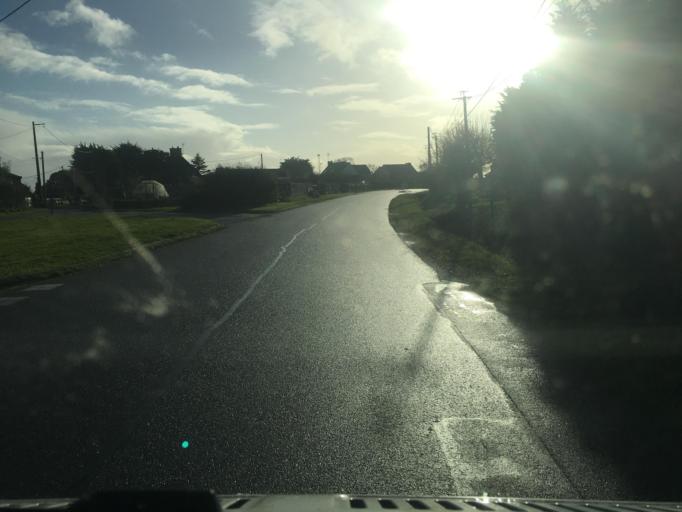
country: FR
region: Brittany
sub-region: Departement du Morbihan
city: Surzur
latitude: 47.5225
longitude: -2.6540
